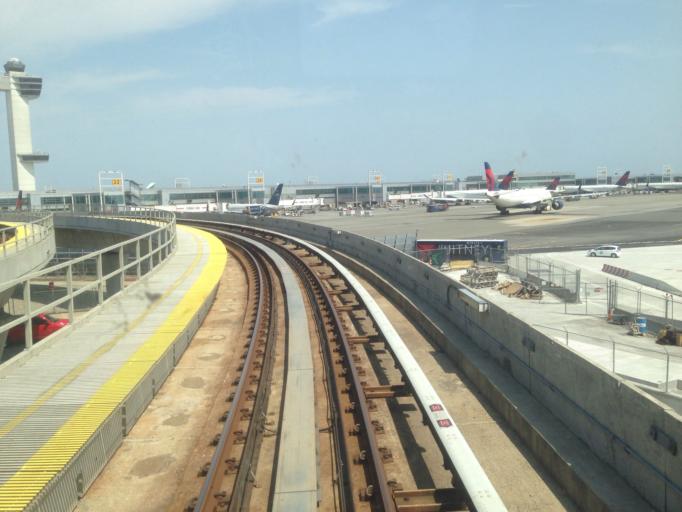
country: US
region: New York
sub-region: Nassau County
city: Inwood
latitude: 40.6419
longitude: -73.7866
